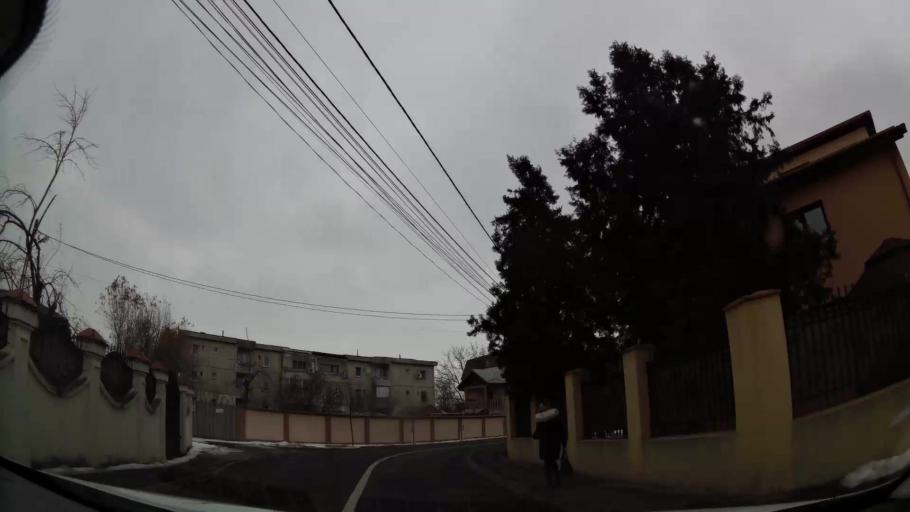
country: RO
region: Ilfov
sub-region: Comuna Otopeni
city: Otopeni
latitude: 44.5486
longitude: 26.0756
